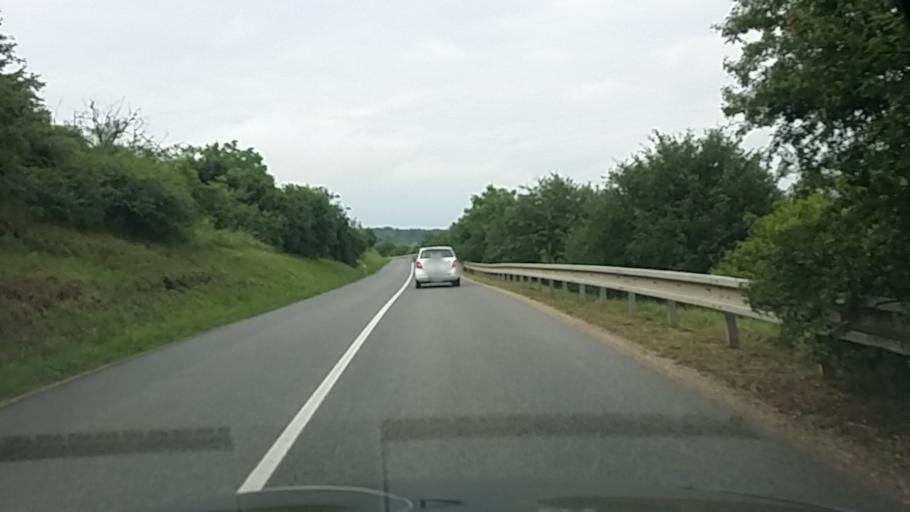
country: SK
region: Nitriansky
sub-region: Okres Nove Zamky
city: Sturovo
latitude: 47.8522
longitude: 18.7301
